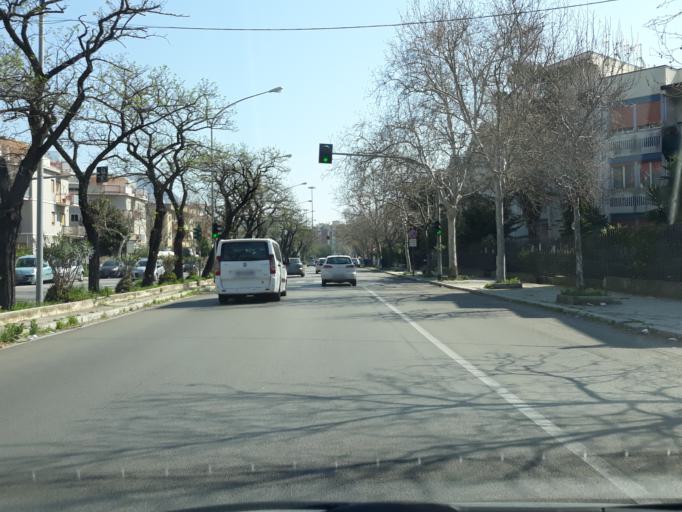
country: IT
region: Sicily
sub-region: Palermo
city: Palermo
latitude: 38.1387
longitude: 13.3267
